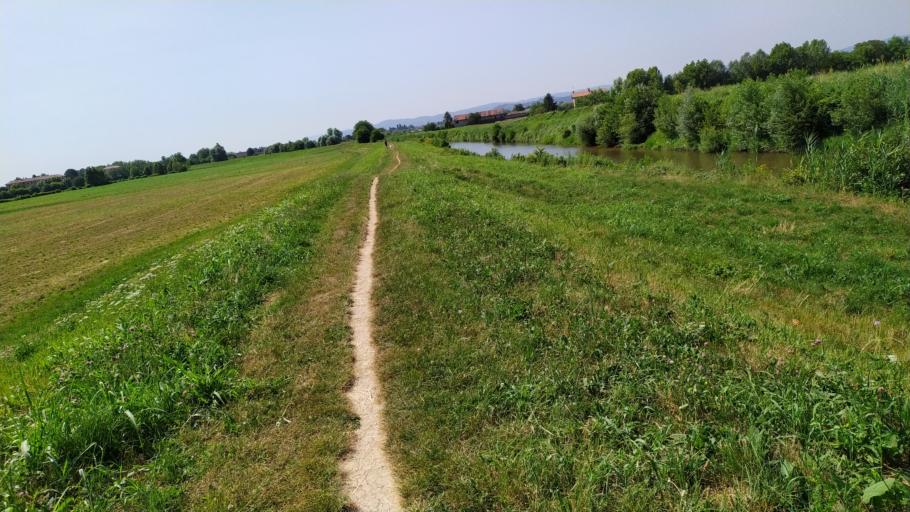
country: IT
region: Veneto
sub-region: Provincia di Vicenza
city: Monticello Conte Otto
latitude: 45.5961
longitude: 11.5370
